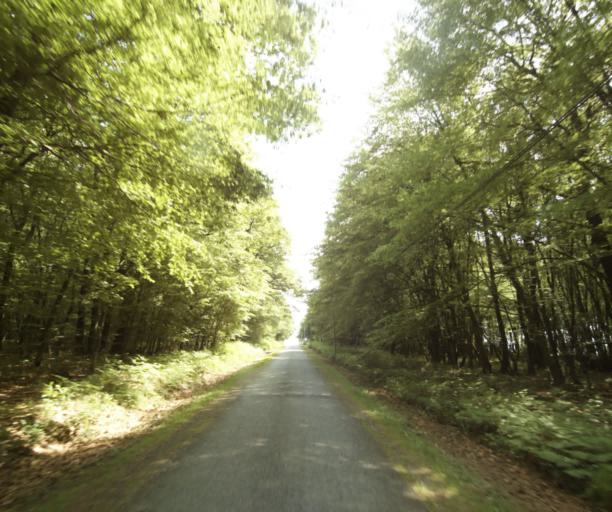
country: FR
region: Bourgogne
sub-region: Departement de Saone-et-Loire
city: Gueugnon
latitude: 46.5926
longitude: 4.1367
